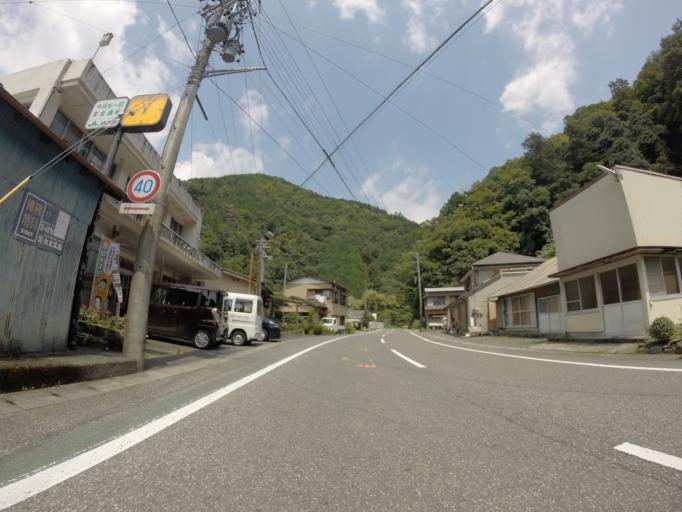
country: JP
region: Shizuoka
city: Shizuoka-shi
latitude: 35.2373
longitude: 138.3419
